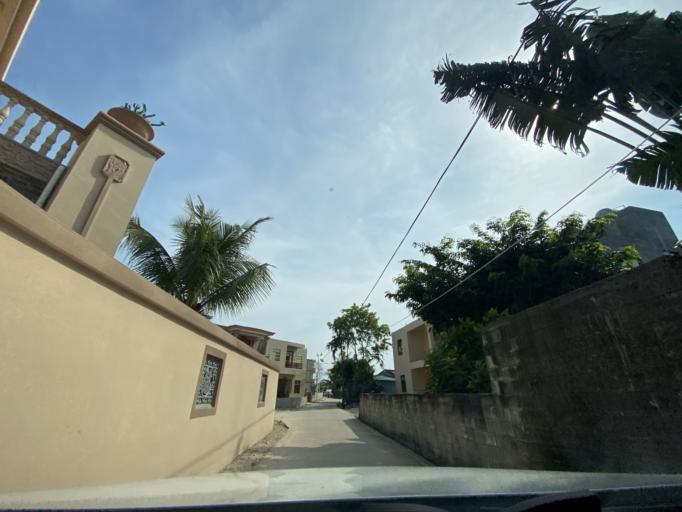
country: CN
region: Hainan
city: Yingzhou
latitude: 18.4079
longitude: 109.8314
